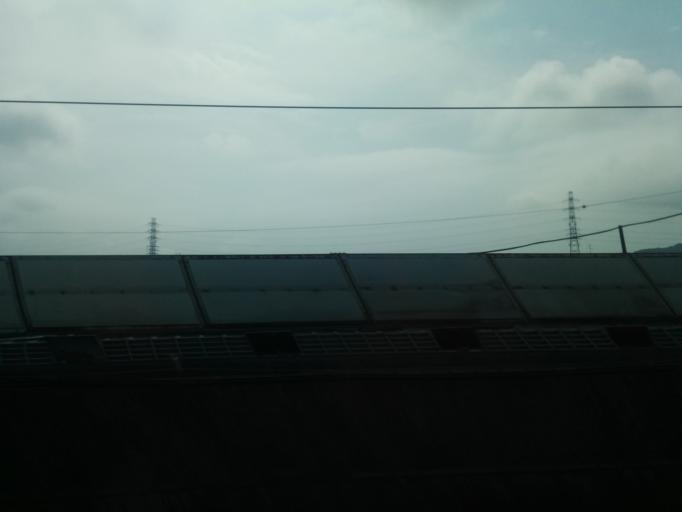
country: JP
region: Kanagawa
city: Hiratsuka
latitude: 35.3476
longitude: 139.3126
